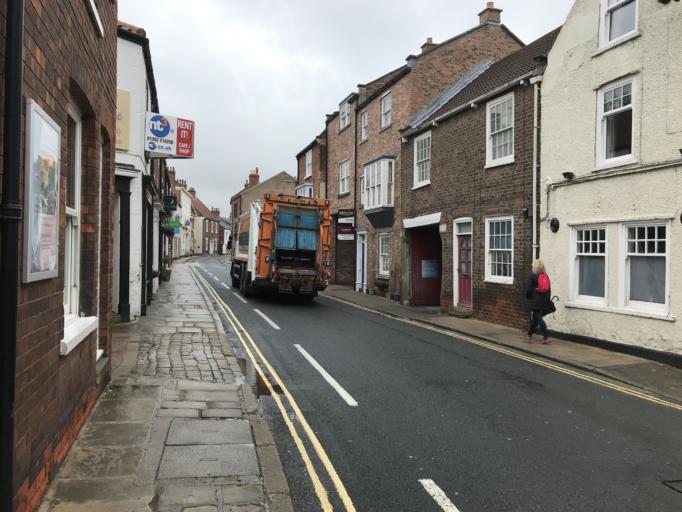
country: GB
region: England
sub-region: East Riding of Yorkshire
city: Beverley
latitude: 53.8416
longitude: -0.4321
